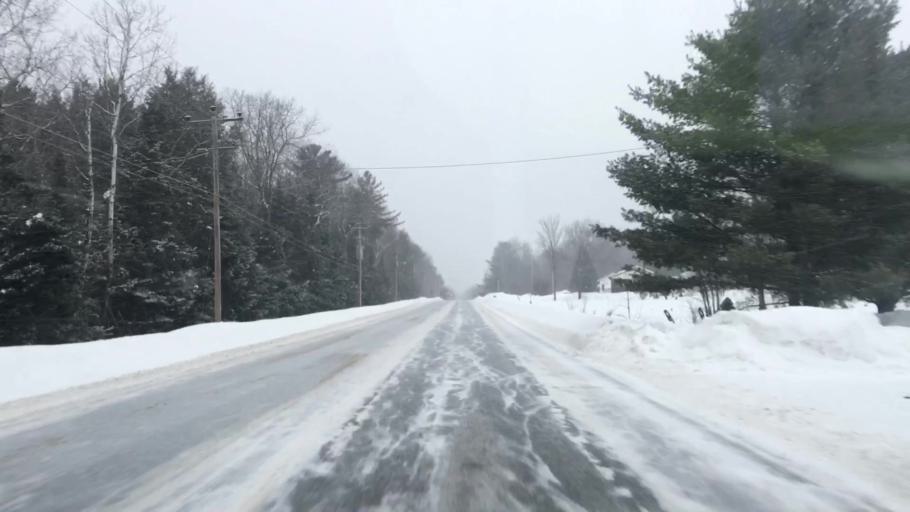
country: US
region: Maine
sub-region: Penobscot County
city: Medway
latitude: 45.5470
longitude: -68.3746
